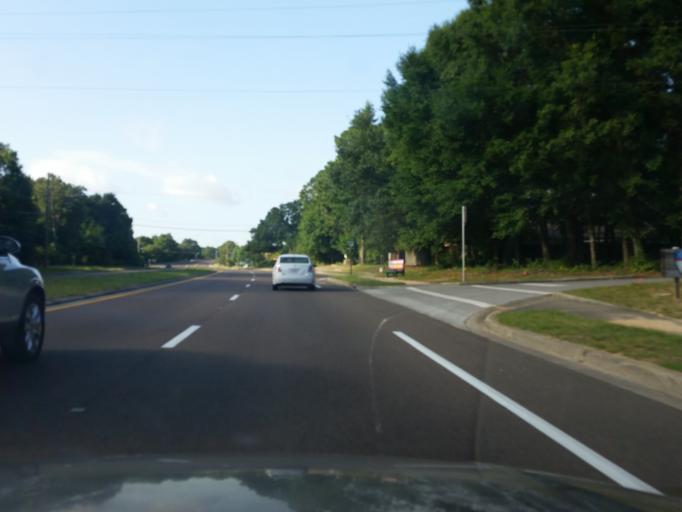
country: US
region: Florida
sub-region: Escambia County
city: Ferry Pass
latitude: 30.5073
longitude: -87.1845
